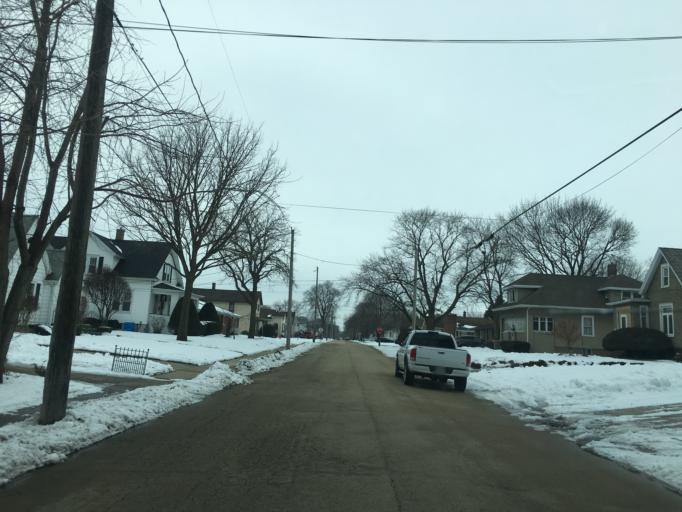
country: US
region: Illinois
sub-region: LaSalle County
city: Peru
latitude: 41.3303
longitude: -89.1334
